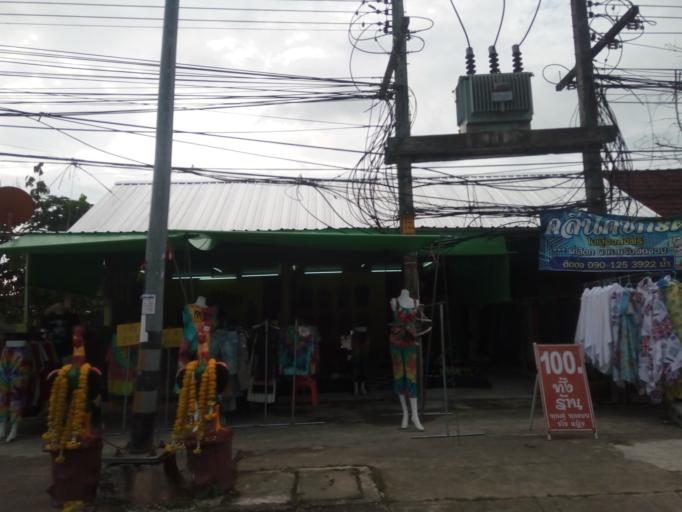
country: TH
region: Phuket
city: Mueang Phuket
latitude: 7.8581
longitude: 98.3803
